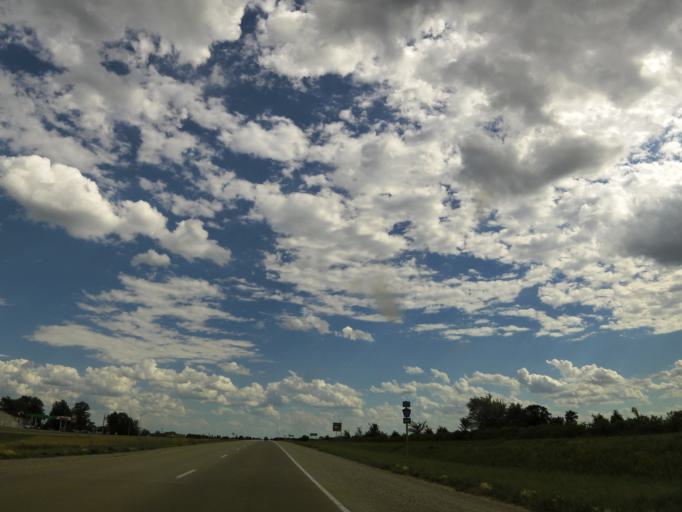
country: US
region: Iowa
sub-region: Henry County
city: Mount Pleasant
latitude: 40.8491
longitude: -91.5651
